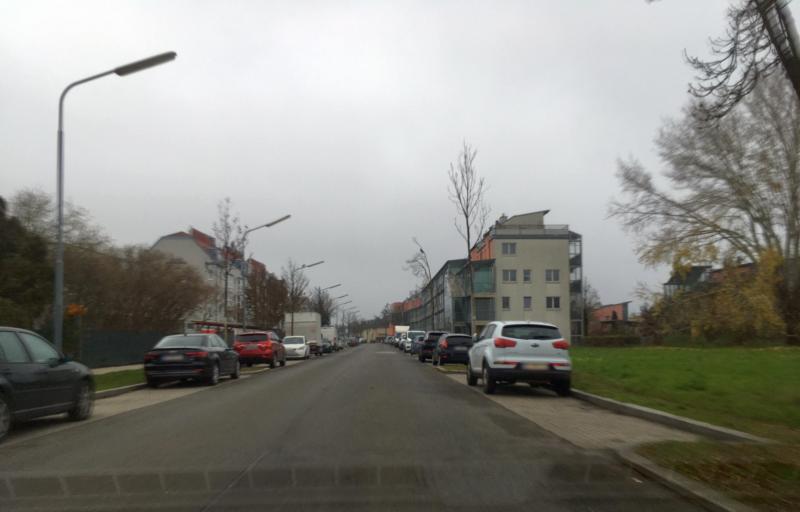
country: AT
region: Lower Austria
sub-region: Politischer Bezirk Ganserndorf
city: Gross-Enzersdorf
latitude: 48.2136
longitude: 16.4736
